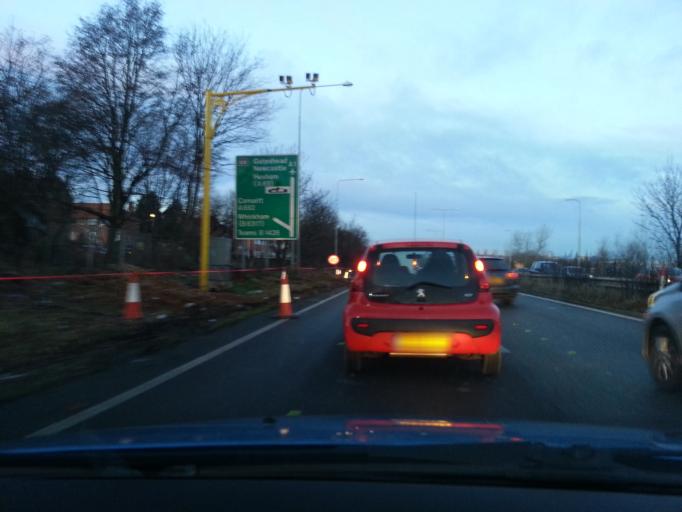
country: GB
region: England
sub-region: Gateshead
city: Lamesley
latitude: 54.9372
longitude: -1.6296
